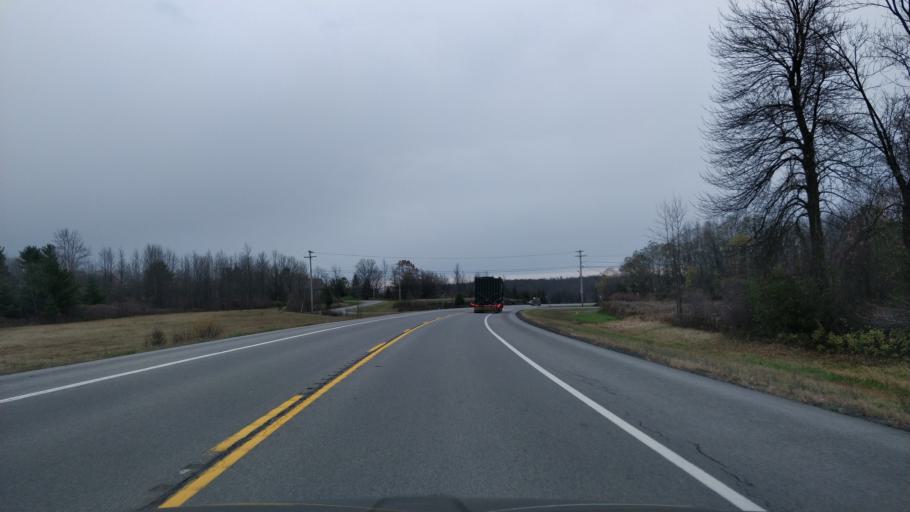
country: CA
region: Ontario
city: Brockville
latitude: 44.5848
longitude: -75.6391
